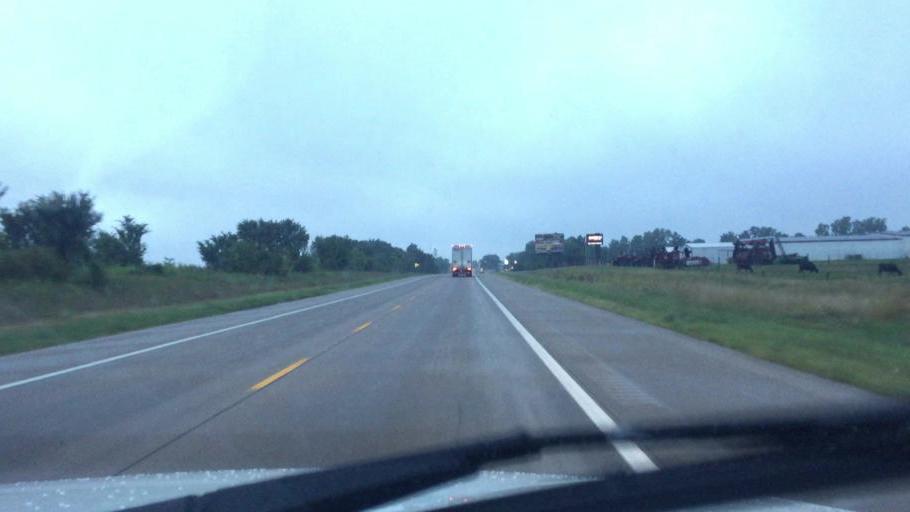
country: US
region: Kansas
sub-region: Neosho County
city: Chanute
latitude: 37.4991
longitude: -95.4706
